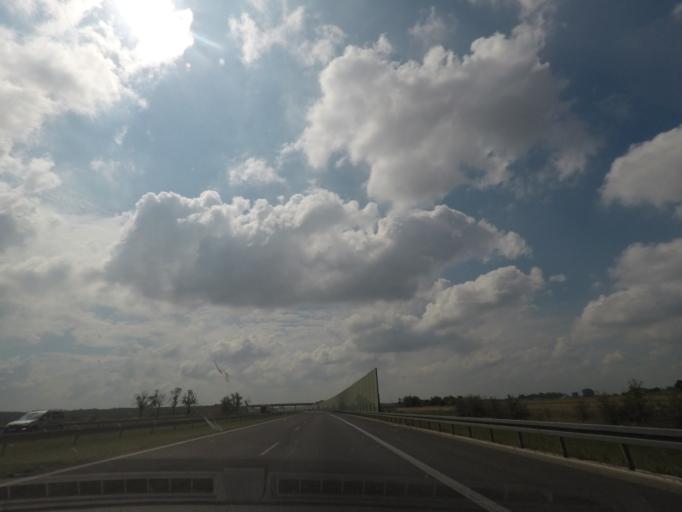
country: PL
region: Lodz Voivodeship
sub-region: Powiat kutnowski
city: Krzyzanow
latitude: 52.1518
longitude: 19.4813
